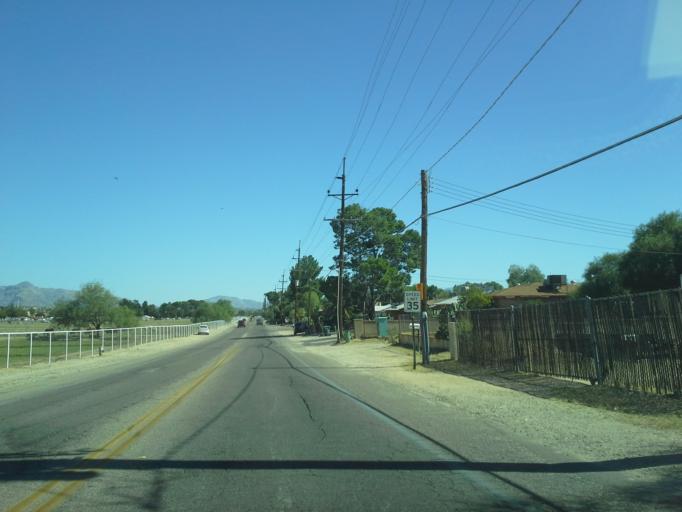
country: US
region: Arizona
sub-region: Pima County
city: Catalina Foothills
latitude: 32.2794
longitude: -110.9517
